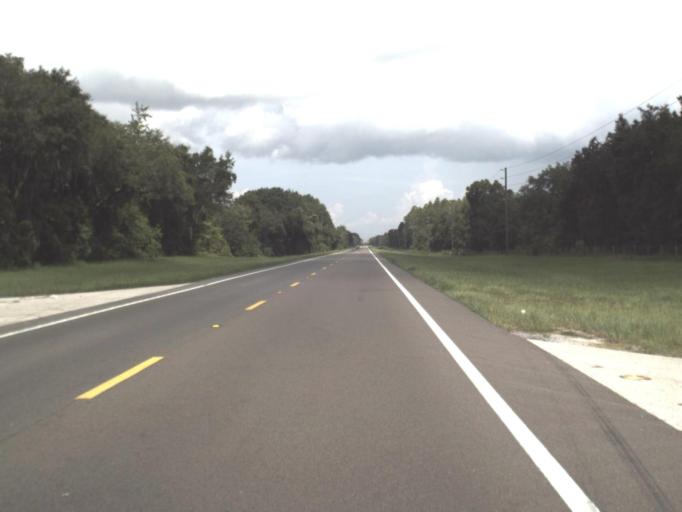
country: US
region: Florida
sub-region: Pasco County
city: Zephyrhills North
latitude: 28.2819
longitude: -82.1162
